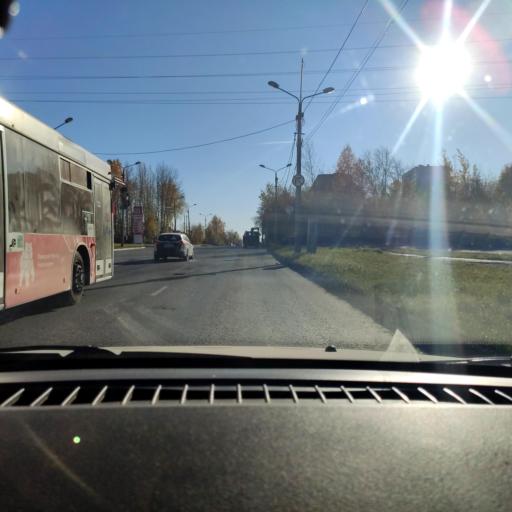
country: RU
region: Perm
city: Perm
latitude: 58.0661
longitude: 56.3653
